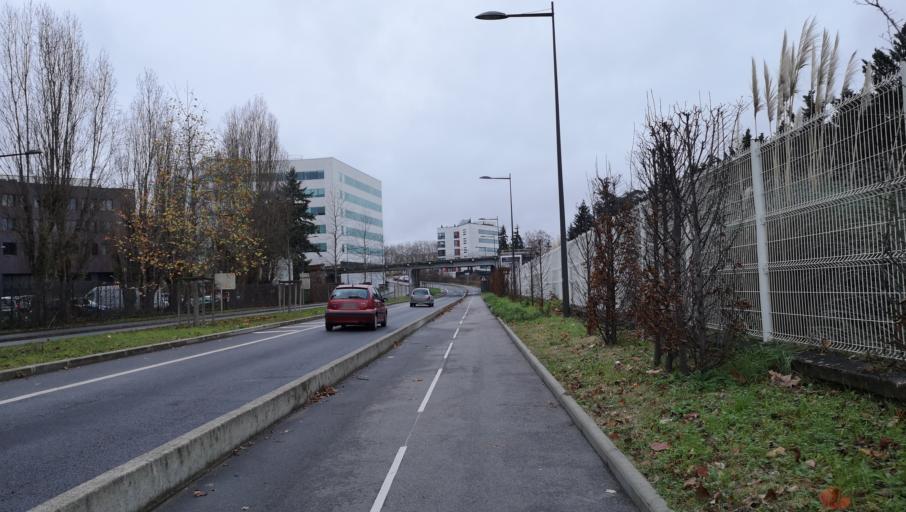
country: FR
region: Centre
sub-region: Departement du Loiret
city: Orleans
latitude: 47.9151
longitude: 1.9040
